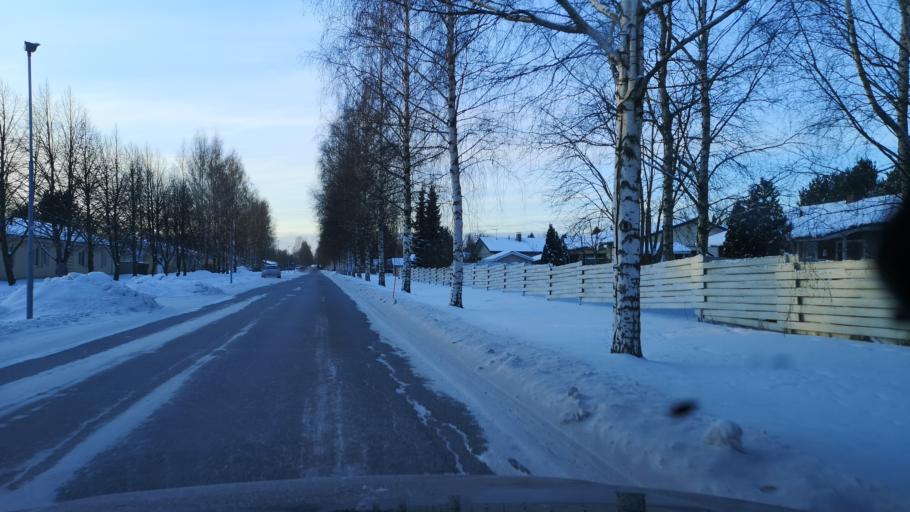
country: FI
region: Satakunta
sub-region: Pori
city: Pori
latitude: 61.5036
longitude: 21.8255
